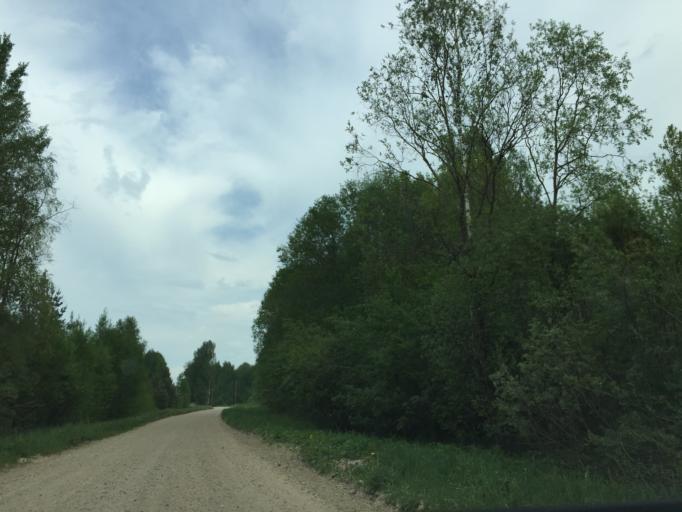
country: LV
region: Livani
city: Livani
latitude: 56.5538
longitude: 26.1030
